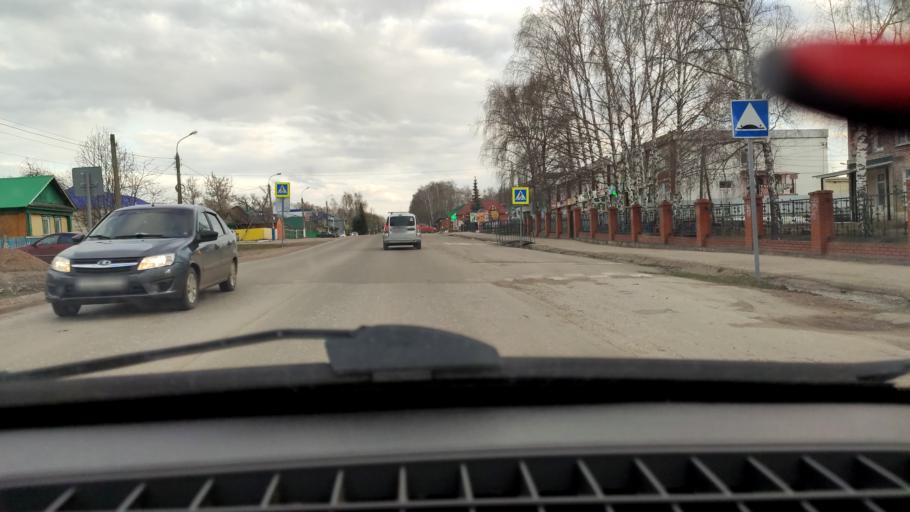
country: RU
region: Bashkortostan
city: Tolbazy
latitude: 54.0191
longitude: 55.8864
